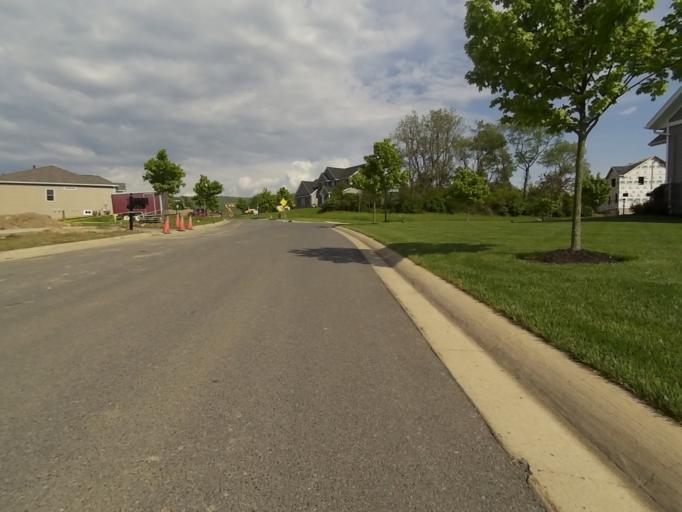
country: US
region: Pennsylvania
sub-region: Centre County
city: Houserville
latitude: 40.8327
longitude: -77.8252
